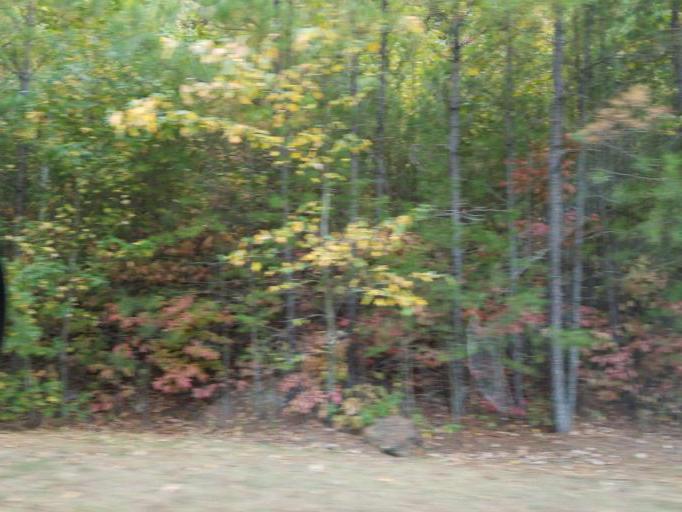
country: US
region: Georgia
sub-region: Bartow County
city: Cartersville
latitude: 34.1754
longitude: -84.7554
